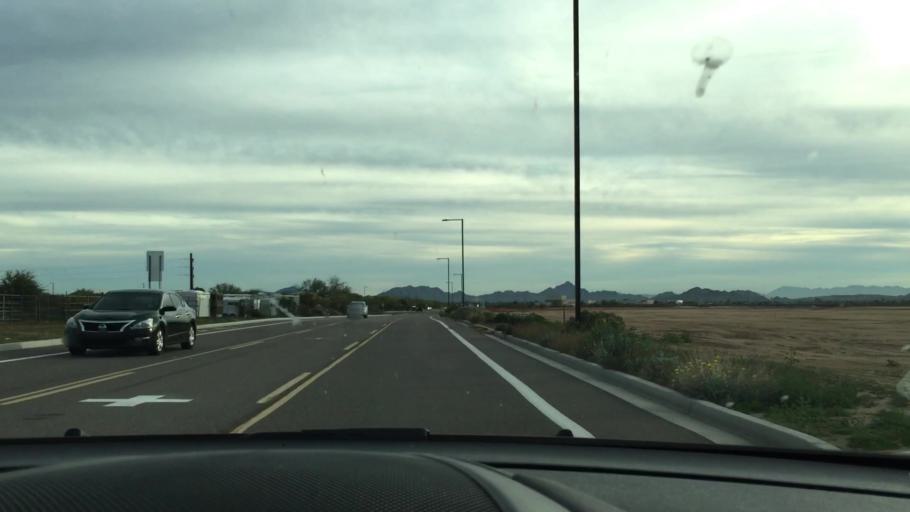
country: US
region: Arizona
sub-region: Maricopa County
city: Cave Creek
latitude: 33.6939
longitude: -112.0056
